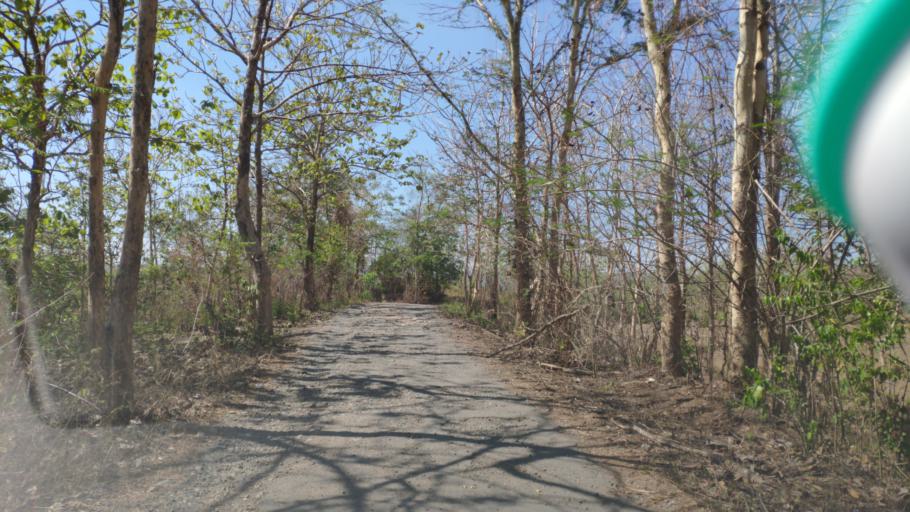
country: ID
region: East Java
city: Krajan Jamprong
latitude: -7.0005
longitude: 111.6046
